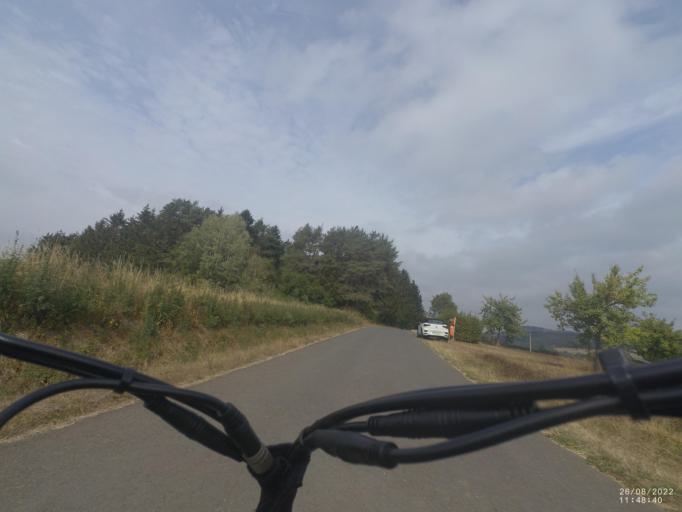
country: DE
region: Rheinland-Pfalz
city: Gerolstein
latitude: 50.2180
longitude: 6.6297
